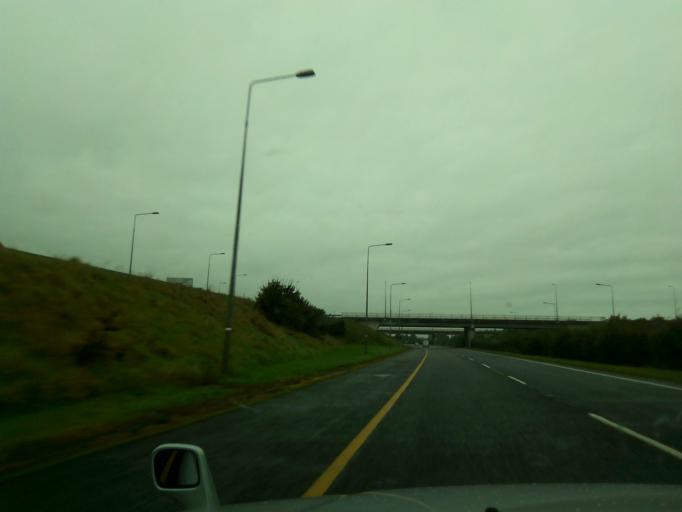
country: IE
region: Leinster
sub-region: Kildare
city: Kilcock
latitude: 53.4006
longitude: -6.6876
